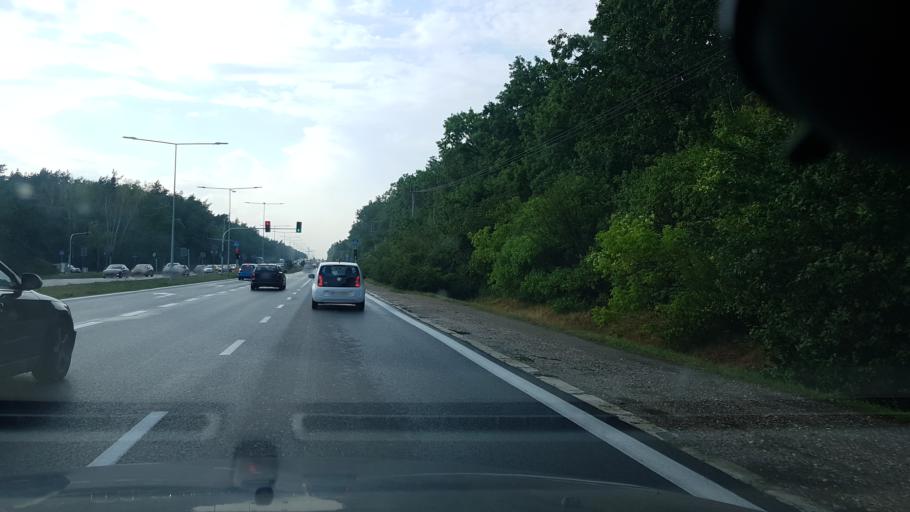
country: PL
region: Masovian Voivodeship
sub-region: Warszawa
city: Bielany
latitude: 52.3135
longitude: 20.9223
